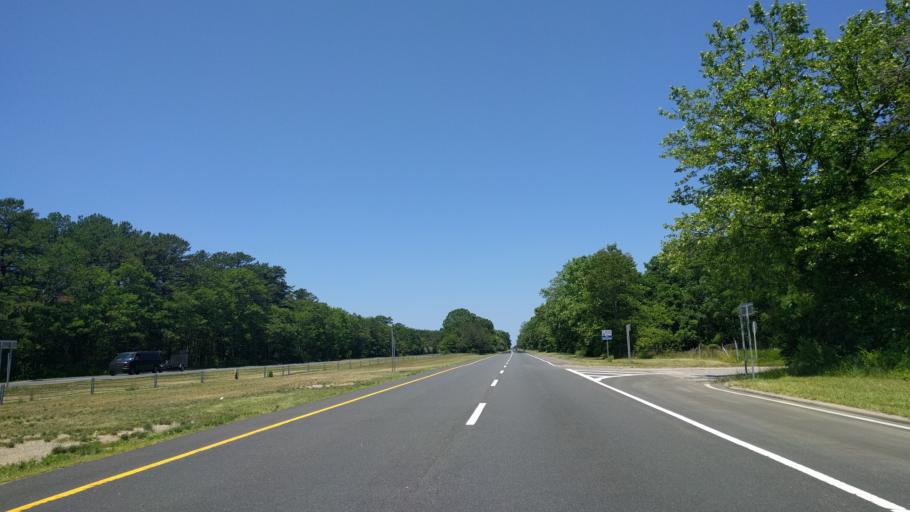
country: US
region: New York
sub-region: Suffolk County
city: Eastport
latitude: 40.8535
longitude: -72.7520
